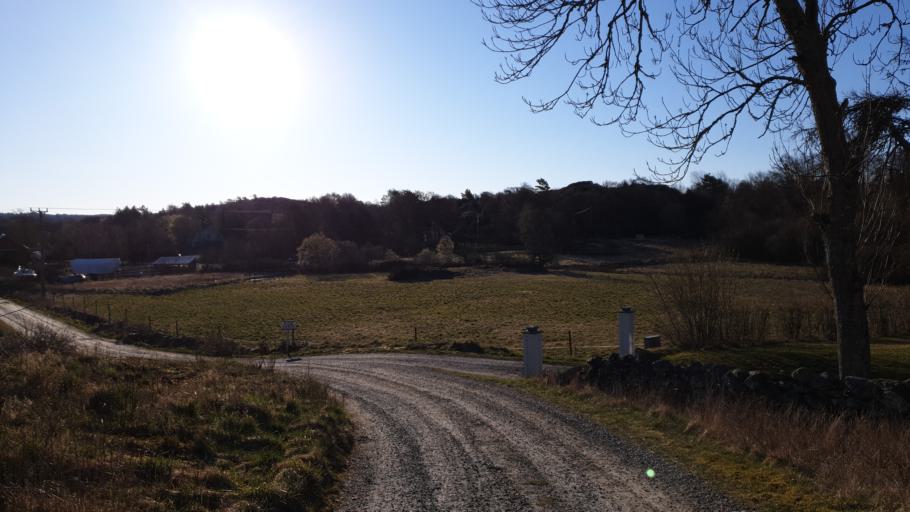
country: SE
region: Vaestra Goetaland
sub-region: Lysekils Kommun
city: Lysekil
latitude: 58.1624
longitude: 11.4378
